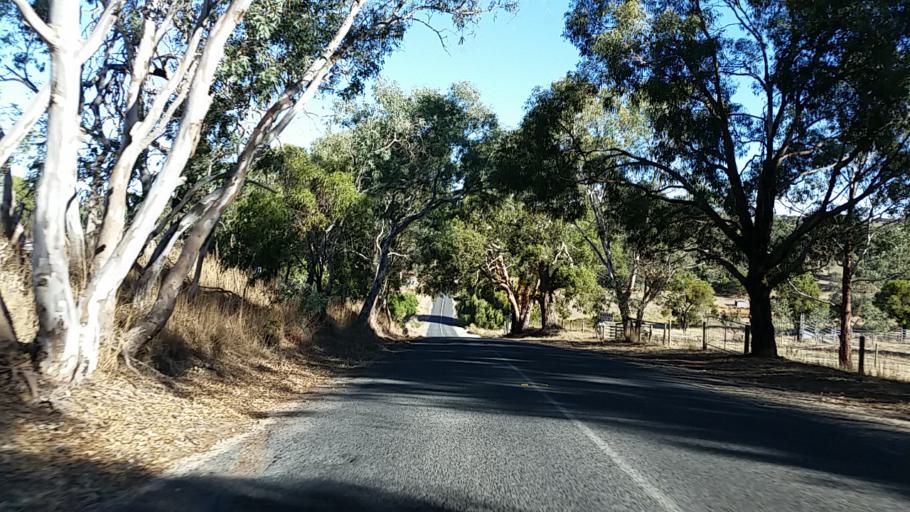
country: AU
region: South Australia
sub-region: Mount Barker
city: Nairne
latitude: -35.0454
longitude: 138.9210
